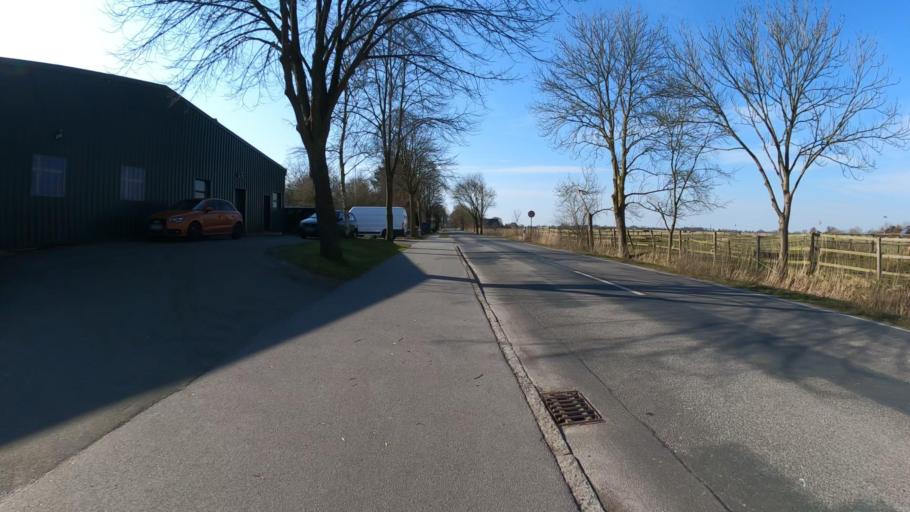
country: DE
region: Schleswig-Holstein
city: Neuendeich
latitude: 53.6756
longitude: 9.6024
